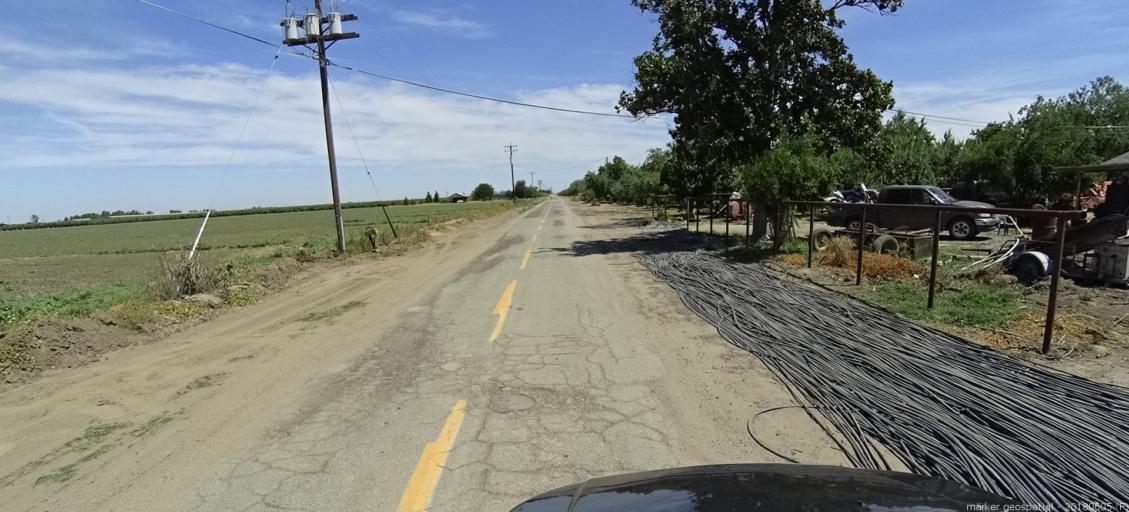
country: US
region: California
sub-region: Madera County
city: Chowchilla
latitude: 37.0878
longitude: -120.4554
